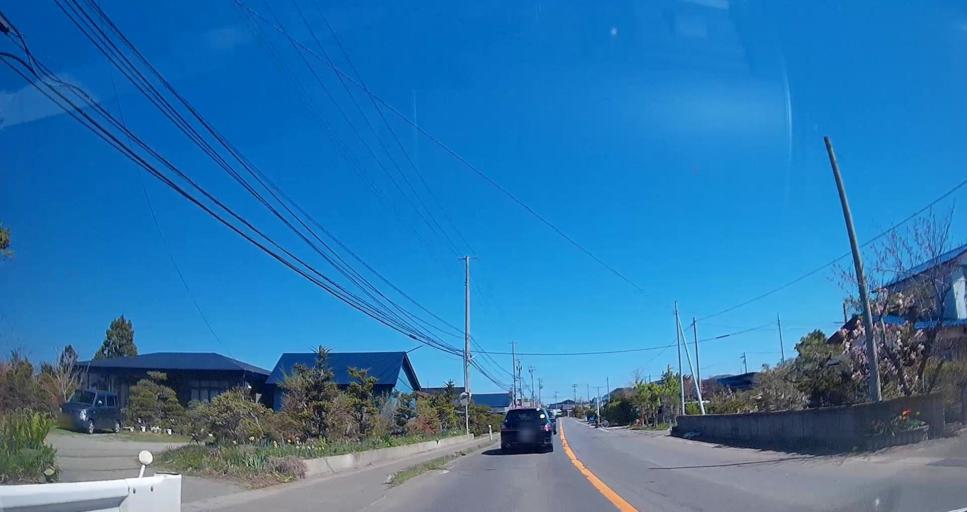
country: JP
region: Aomori
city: Misawa
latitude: 40.7864
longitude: 141.3996
